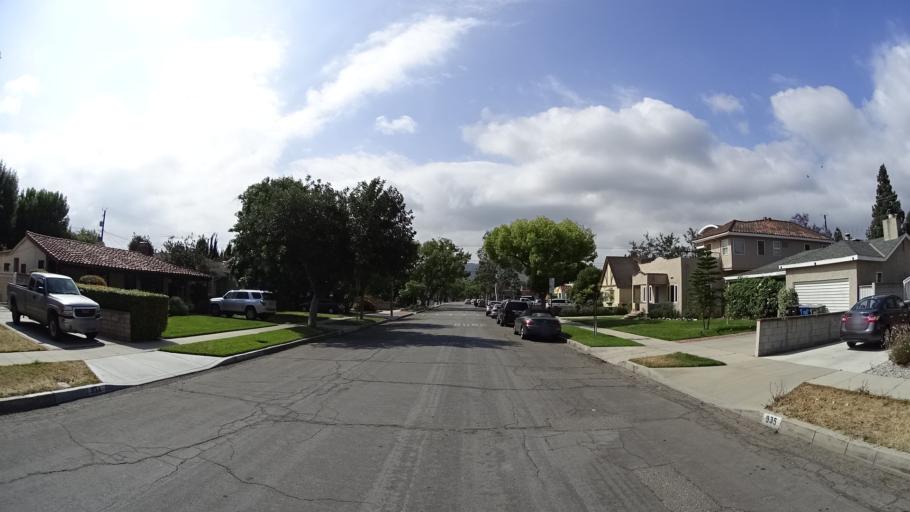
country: US
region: California
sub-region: Los Angeles County
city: Burbank
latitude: 34.1718
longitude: -118.3396
